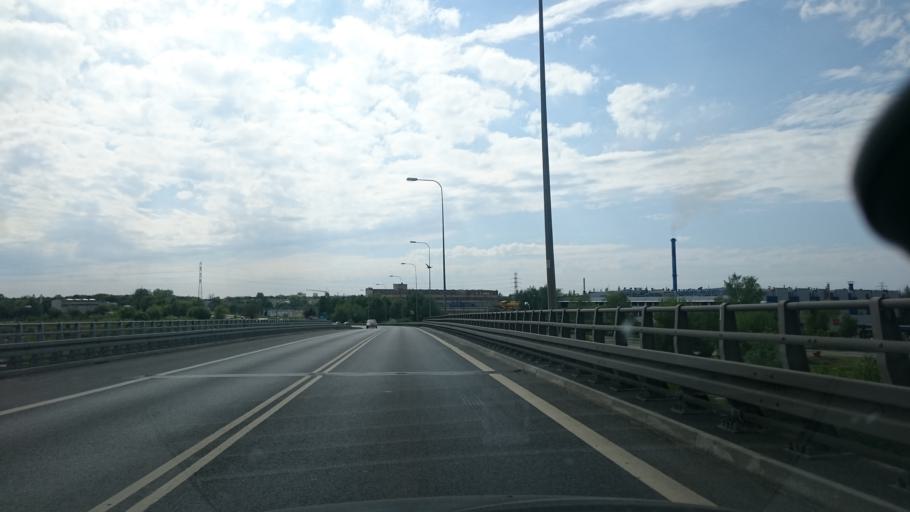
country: PL
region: Kujawsko-Pomorskie
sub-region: Grudziadz
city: Grudziadz
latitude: 53.4794
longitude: 18.7842
